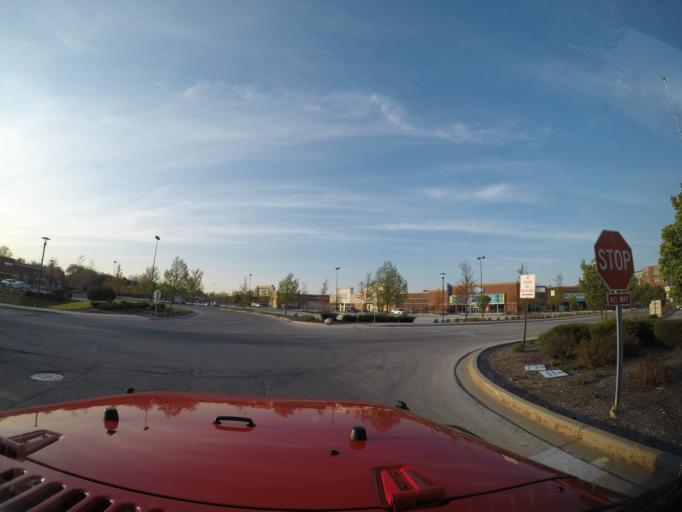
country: US
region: Illinois
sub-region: Cook County
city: Prospect Heights
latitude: 42.0833
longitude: -87.9354
